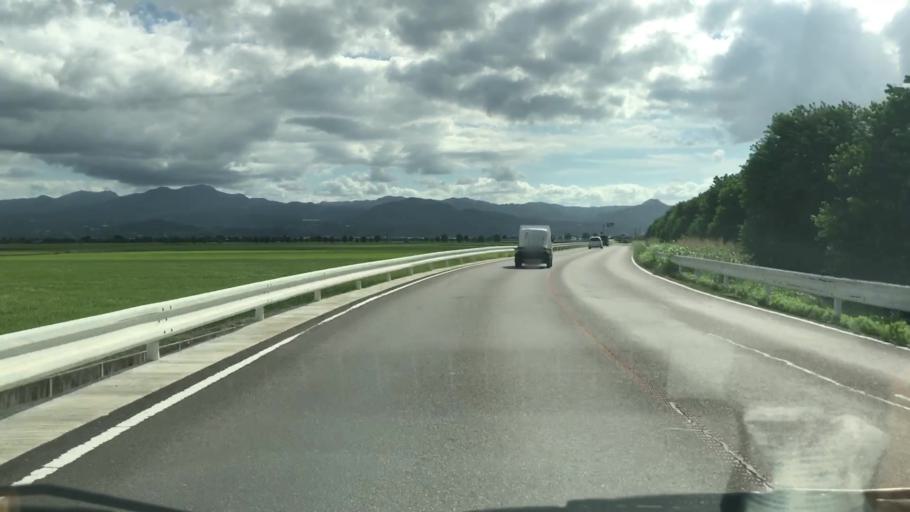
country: JP
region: Saga Prefecture
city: Kashima
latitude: 33.1389
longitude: 130.1428
